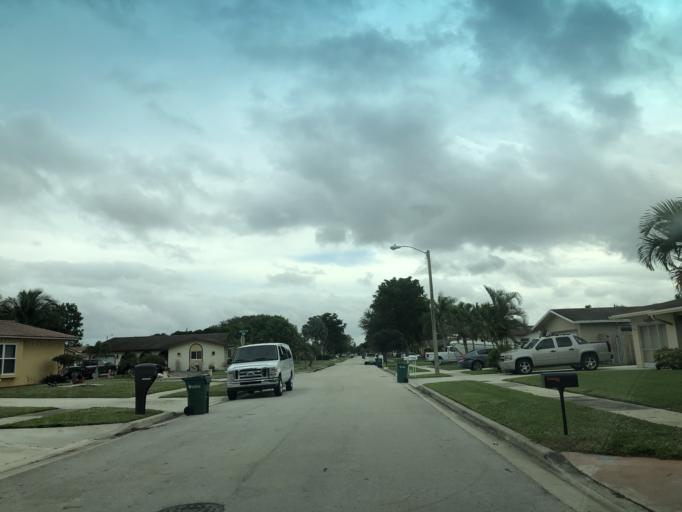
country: US
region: Florida
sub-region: Broward County
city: North Lauderdale
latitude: 26.2421
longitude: -80.2333
